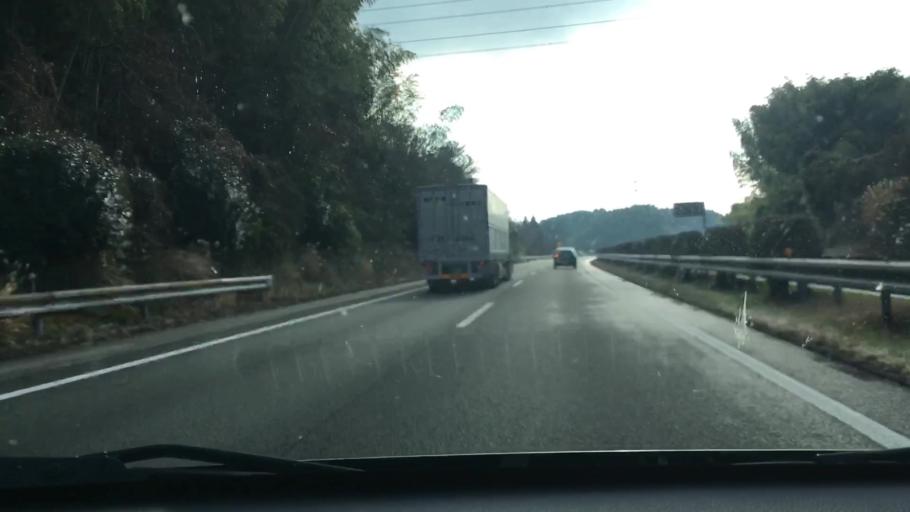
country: JP
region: Kumamoto
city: Uto
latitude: 32.6870
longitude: 130.7359
